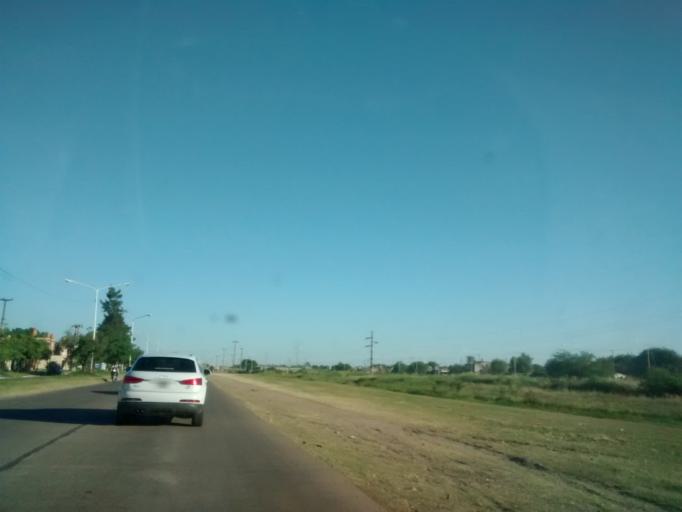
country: AR
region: Chaco
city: Resistencia
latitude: -27.4605
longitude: -59.0192
